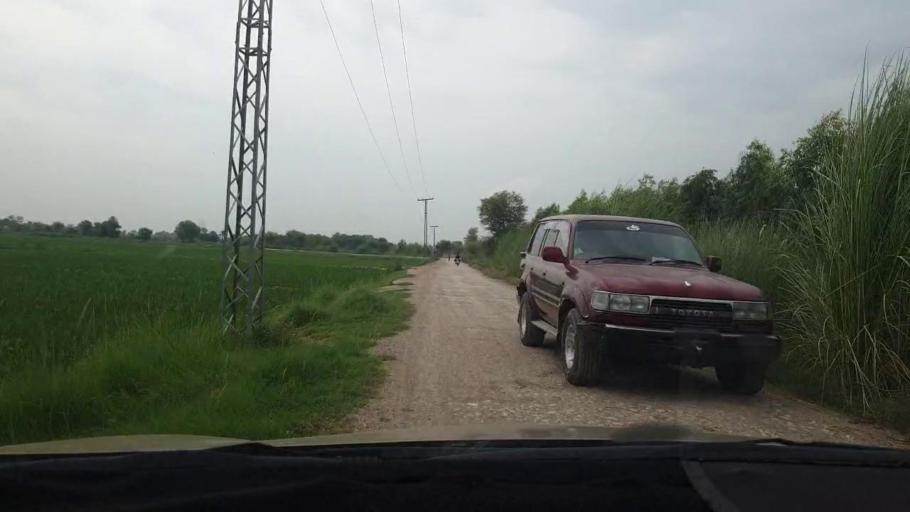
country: PK
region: Sindh
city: Larkana
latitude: 27.5790
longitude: 68.2361
